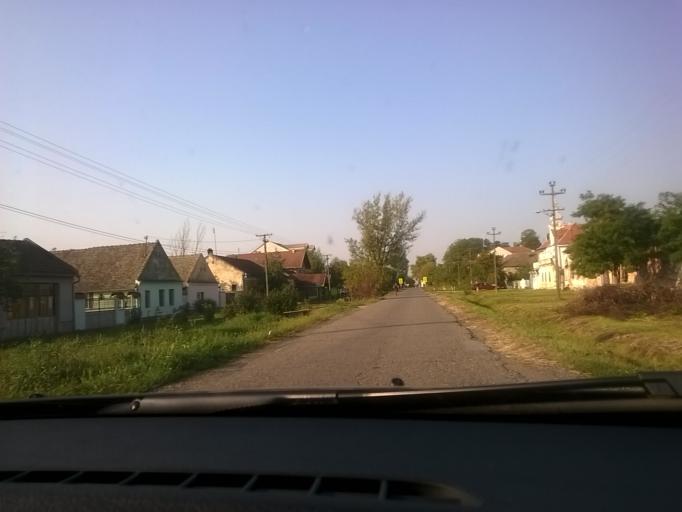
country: RS
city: Pavlis
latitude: 45.1066
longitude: 21.2418
